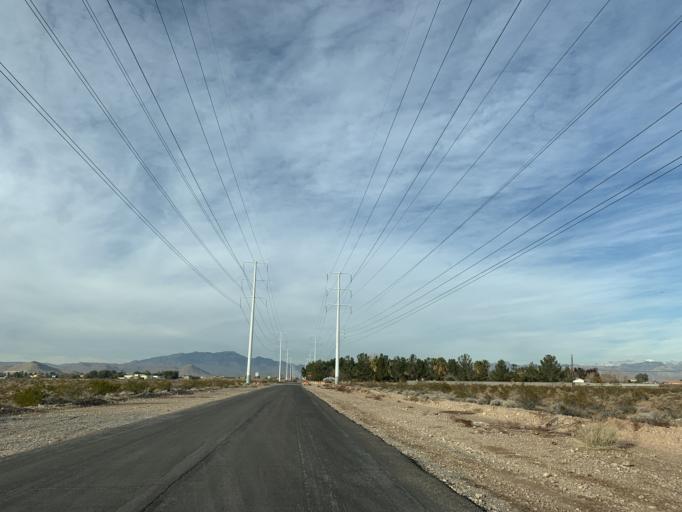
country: US
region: Nevada
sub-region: Clark County
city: Enterprise
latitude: 36.0026
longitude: -115.1877
